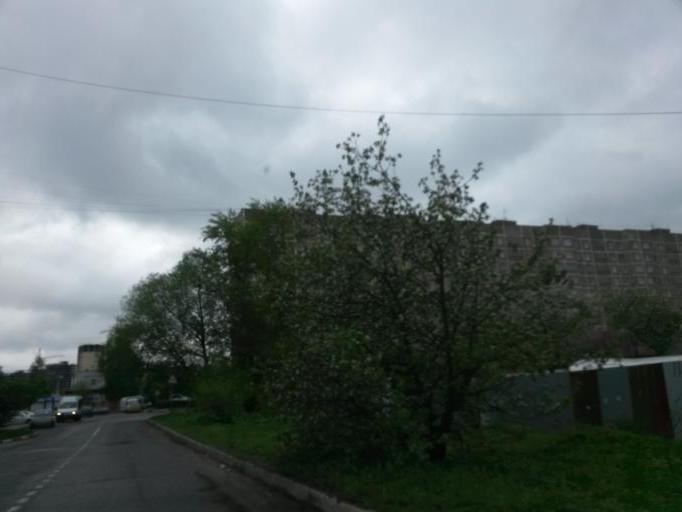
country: RU
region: Moskovskaya
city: Klimovsk
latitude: 55.3600
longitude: 37.5395
